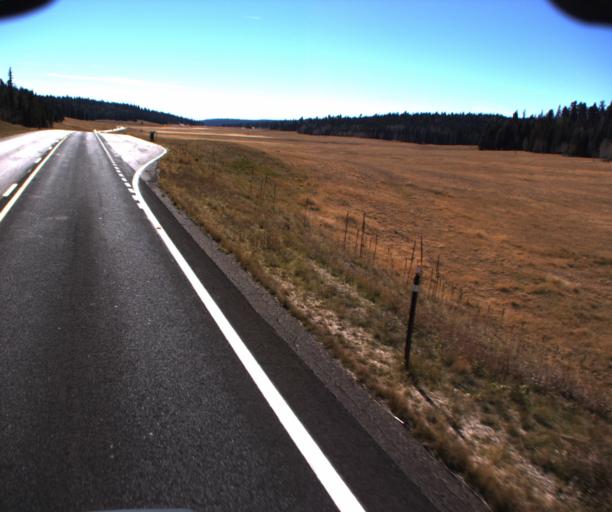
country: US
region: Arizona
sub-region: Coconino County
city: Grand Canyon
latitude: 36.4353
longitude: -112.1339
